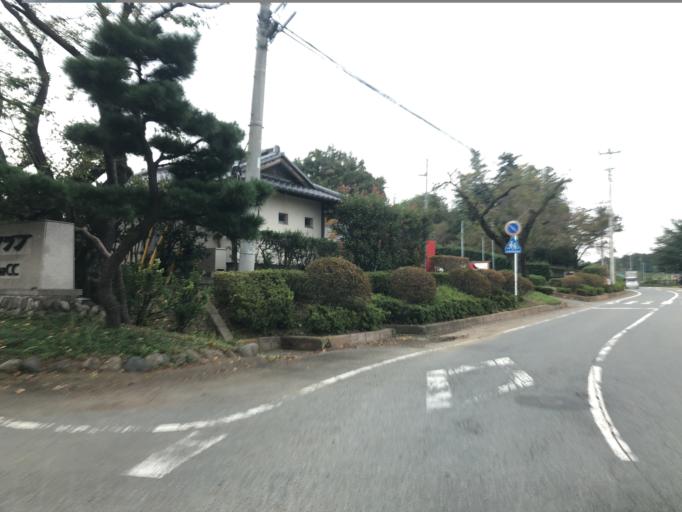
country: JP
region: Saitama
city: Kumagaya
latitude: 36.0643
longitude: 139.3858
